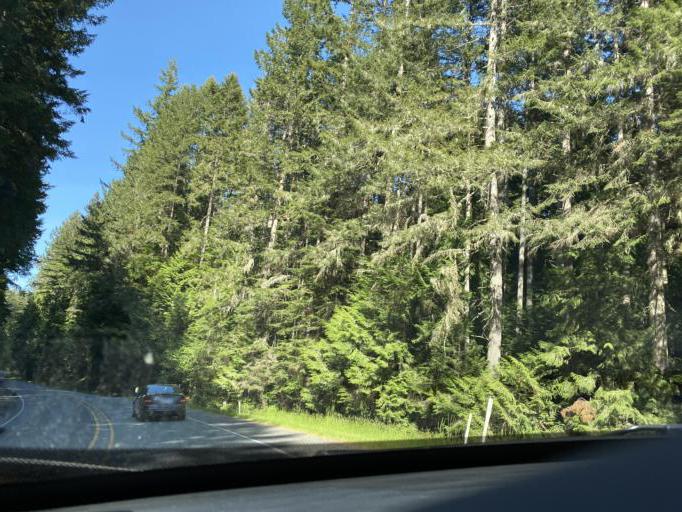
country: US
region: Washington
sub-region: Island County
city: Langley
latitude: 48.0312
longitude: -122.4331
